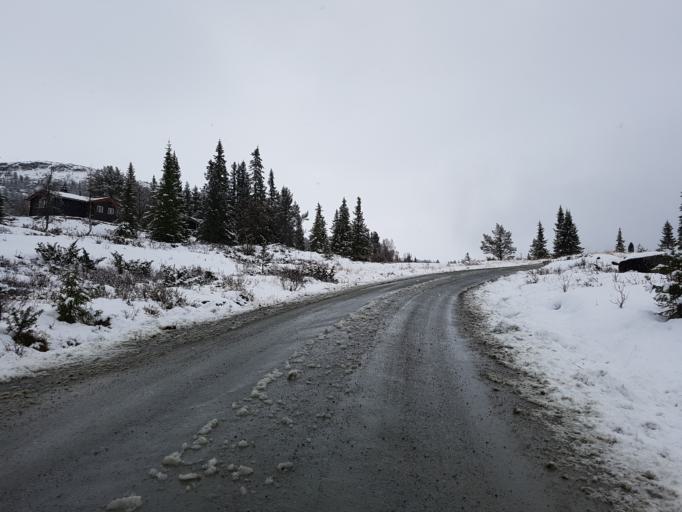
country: NO
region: Oppland
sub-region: Sel
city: Otta
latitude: 61.8057
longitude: 9.6908
